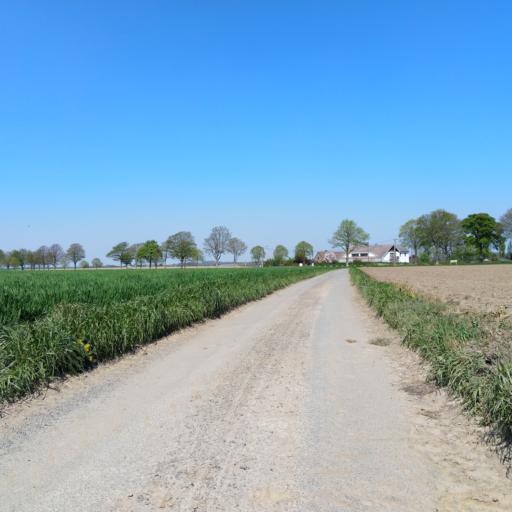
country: BE
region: Wallonia
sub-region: Province du Hainaut
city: Lens
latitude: 50.5651
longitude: 3.8833
